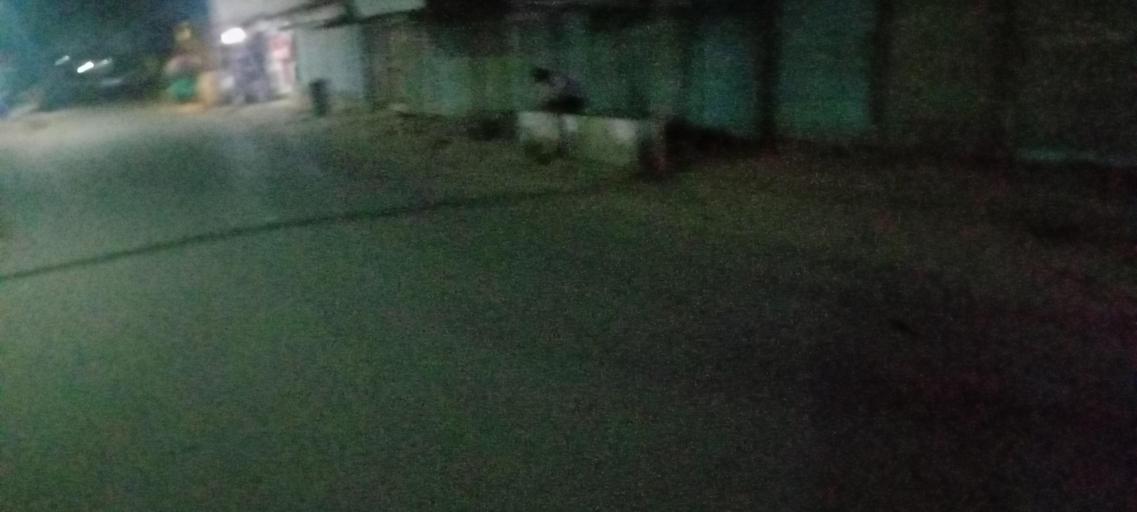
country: BD
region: Dhaka
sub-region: Dhaka
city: Dhaka
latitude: 23.6435
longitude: 90.4158
